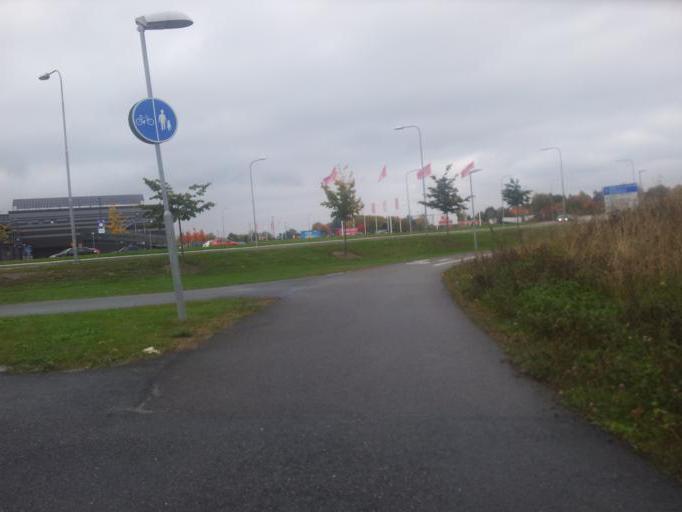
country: SE
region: Uppsala
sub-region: Uppsala Kommun
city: Uppsala
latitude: 59.8753
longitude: 17.6763
